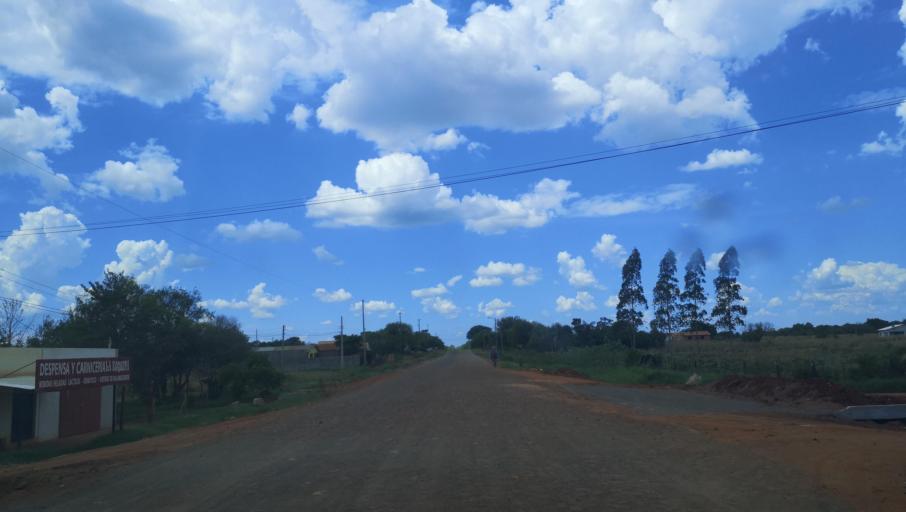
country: PY
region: Misiones
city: Santa Maria
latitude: -26.8957
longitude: -57.0390
